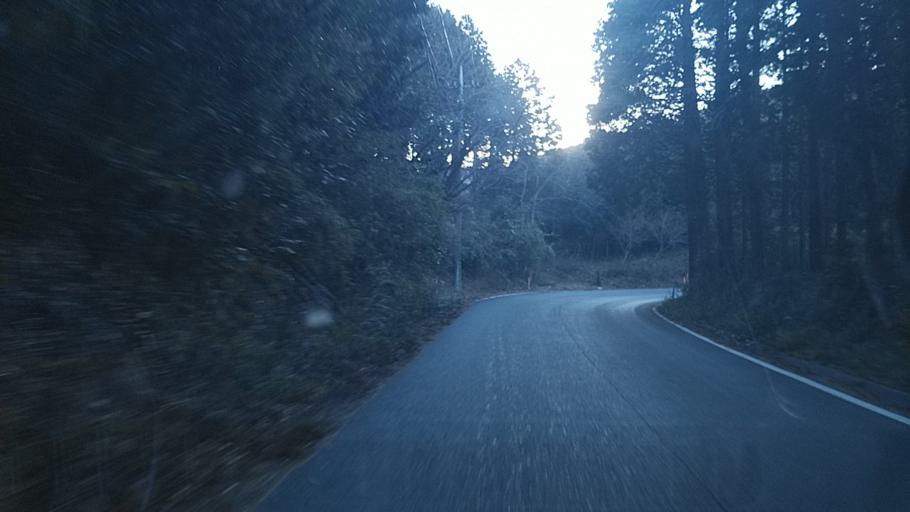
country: JP
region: Chiba
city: Kimitsu
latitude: 35.2570
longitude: 139.9516
